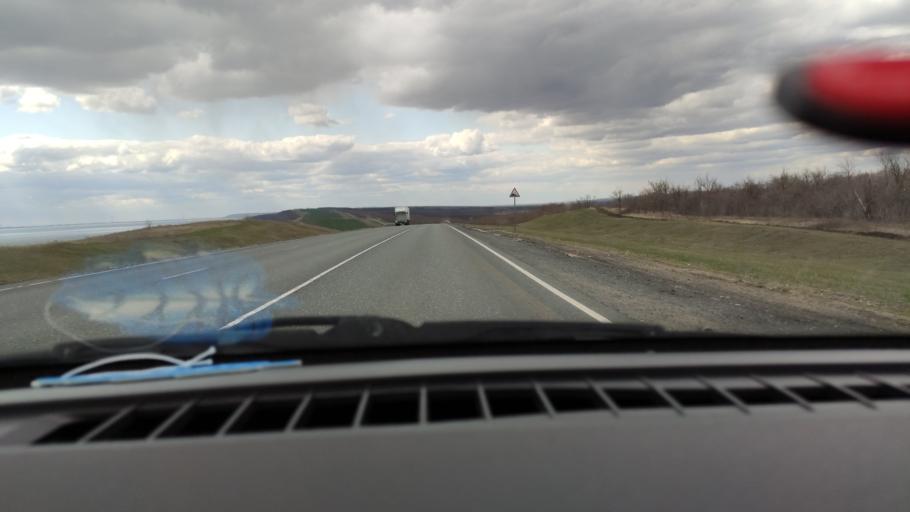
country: RU
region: Saratov
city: Balakovo
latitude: 52.2032
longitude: 47.8682
